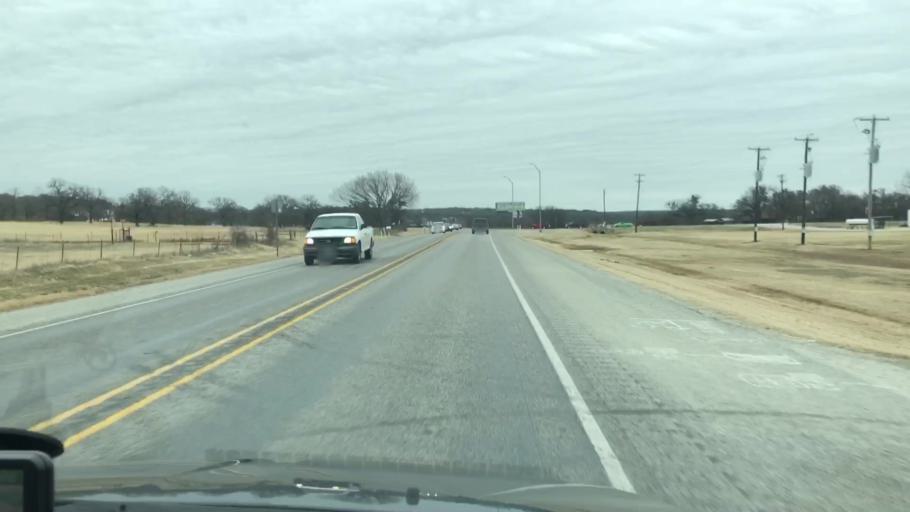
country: US
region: Texas
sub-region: Palo Pinto County
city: Mineral Wells
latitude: 32.8534
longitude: -98.0952
